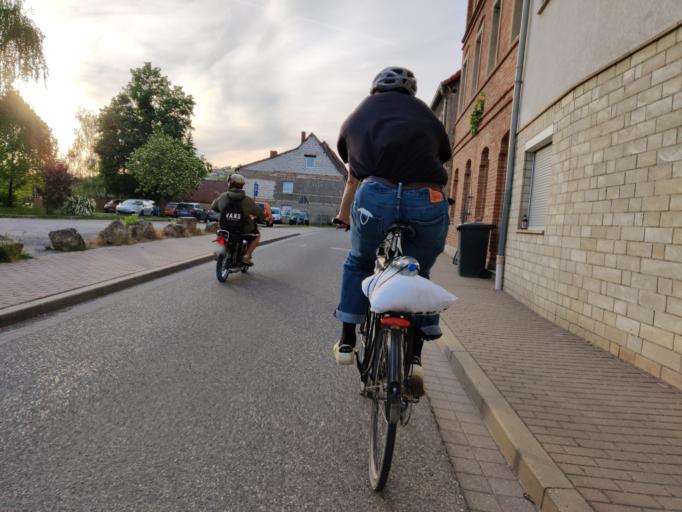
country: DE
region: Saxony-Anhalt
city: Freyburg
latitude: 51.2093
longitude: 11.7711
